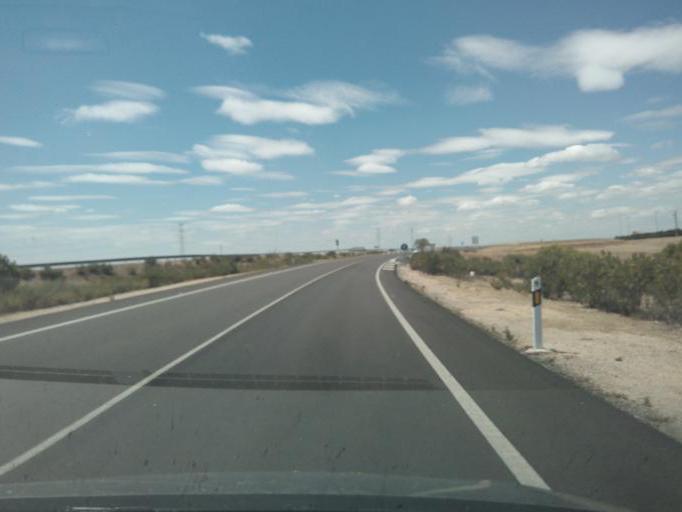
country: ES
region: Madrid
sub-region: Provincia de Madrid
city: Cobena
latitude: 40.5549
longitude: -3.4939
